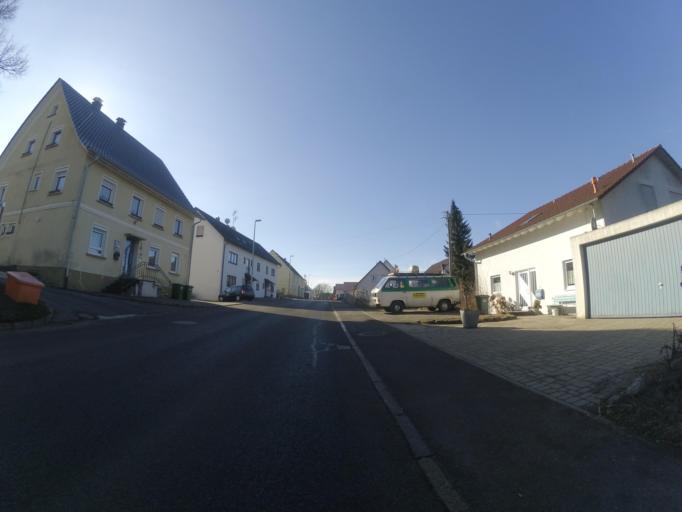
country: DE
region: Baden-Wuerttemberg
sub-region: Tuebingen Region
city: Aulendorf
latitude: 47.9310
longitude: 9.6408
